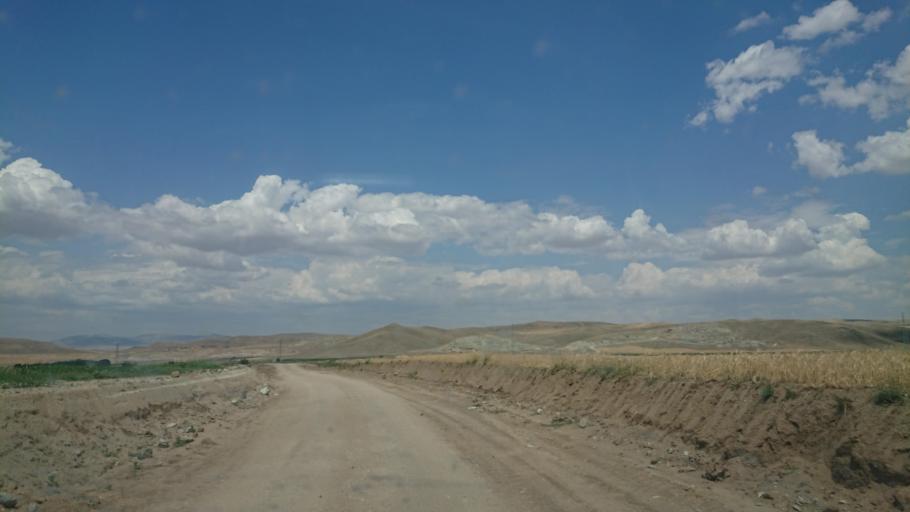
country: TR
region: Aksaray
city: Sariyahsi
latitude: 38.9761
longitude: 33.9006
